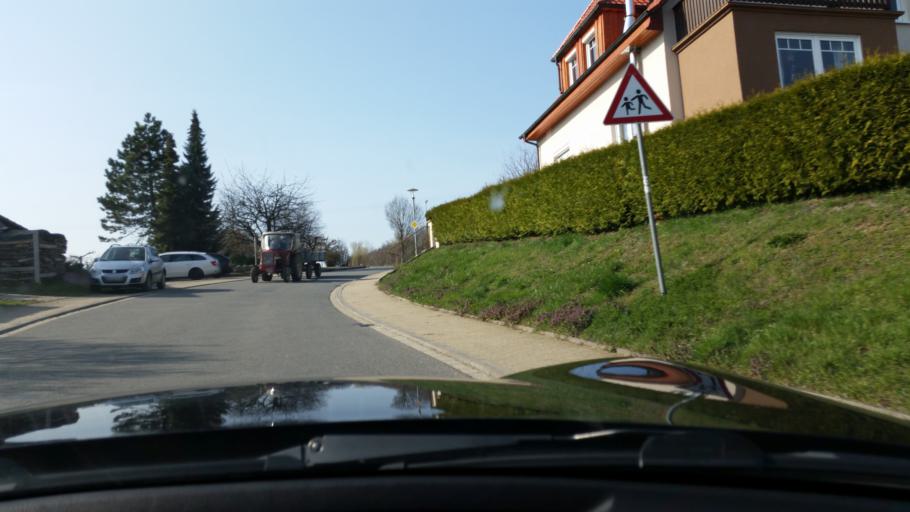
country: DE
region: Baden-Wuerttemberg
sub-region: Karlsruhe Region
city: Billigheim
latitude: 49.3644
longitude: 9.2814
